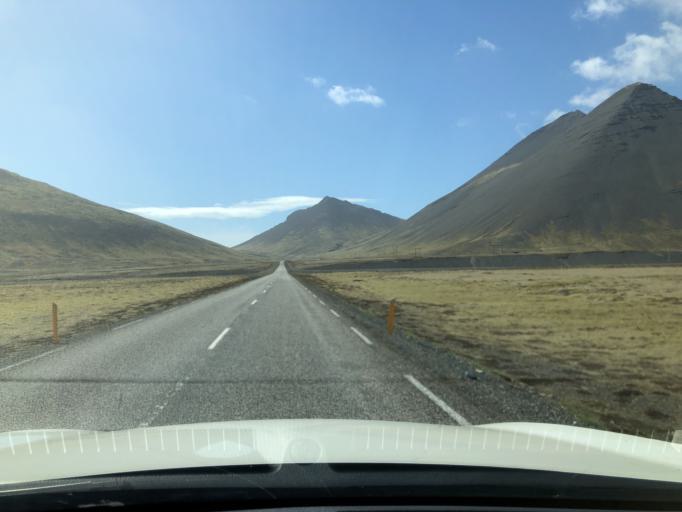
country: IS
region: East
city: Hoefn
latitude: 64.3085
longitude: -14.9875
